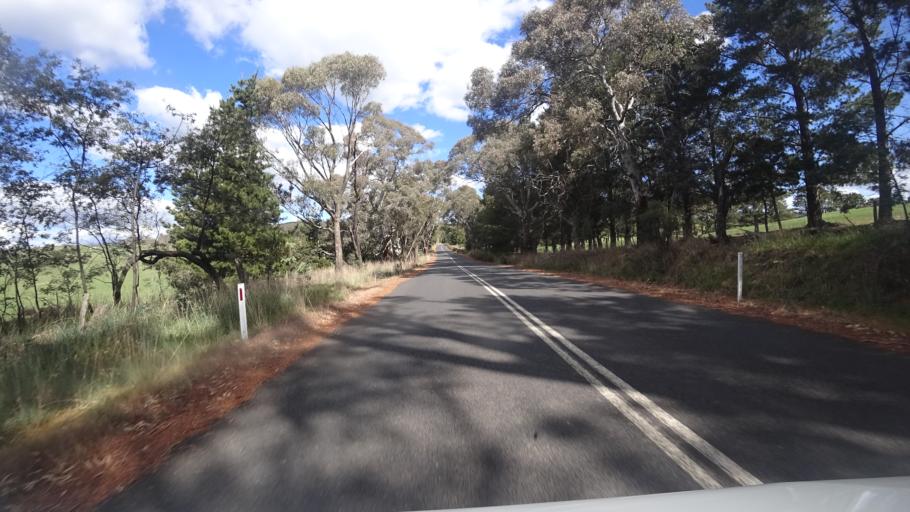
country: AU
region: New South Wales
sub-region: Oberon
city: Oberon
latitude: -33.6774
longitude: 149.7856
